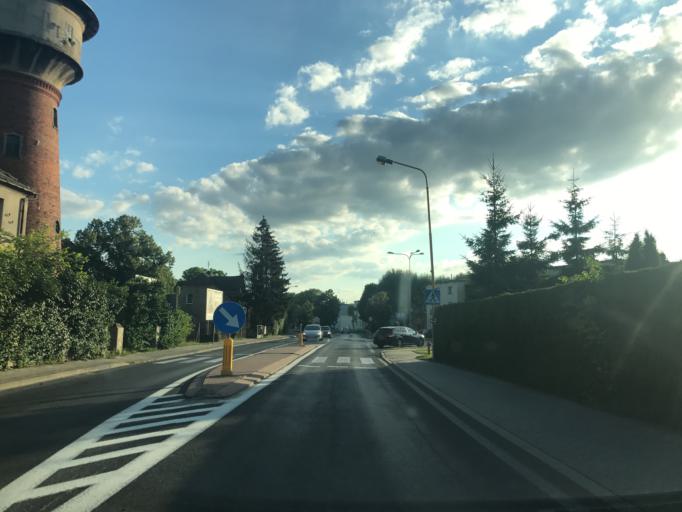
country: PL
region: Greater Poland Voivodeship
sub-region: Powiat jarocinski
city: Jarocin
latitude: 51.9765
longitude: 17.5128
